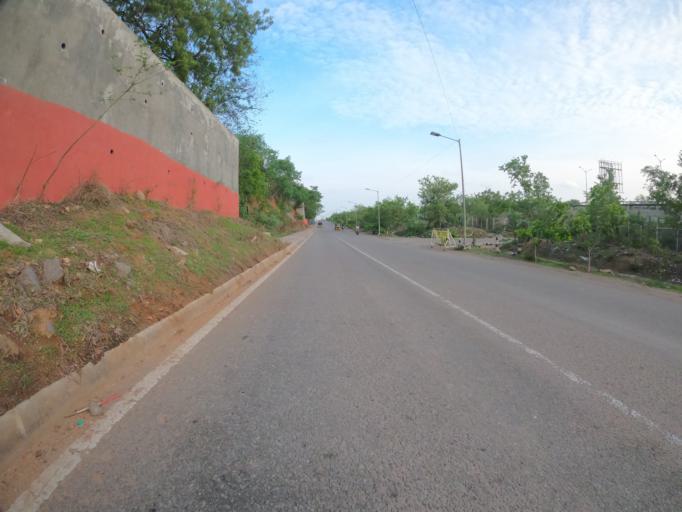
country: IN
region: Telangana
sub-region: Hyderabad
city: Hyderabad
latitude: 17.3547
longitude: 78.3580
